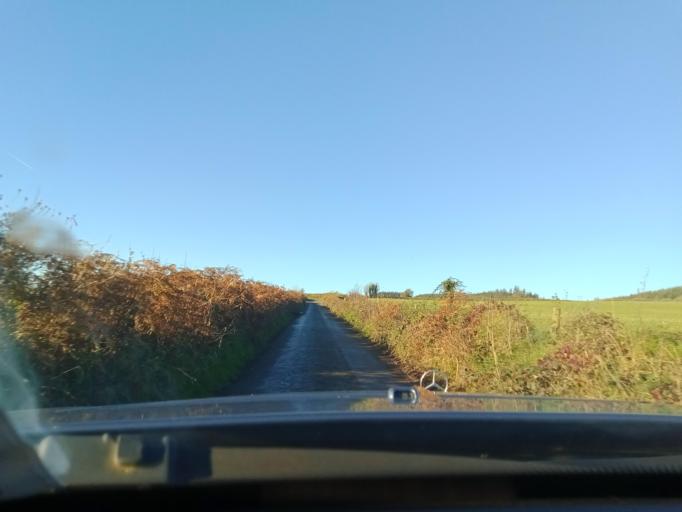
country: IE
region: Leinster
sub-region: Kilkenny
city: Callan
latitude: 52.4610
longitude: -7.4156
